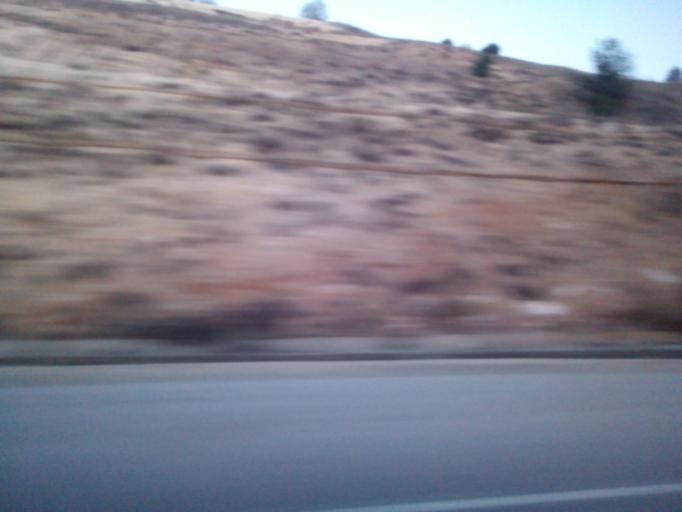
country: TR
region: Ankara
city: Celtikci
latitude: 40.2796
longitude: 32.4861
